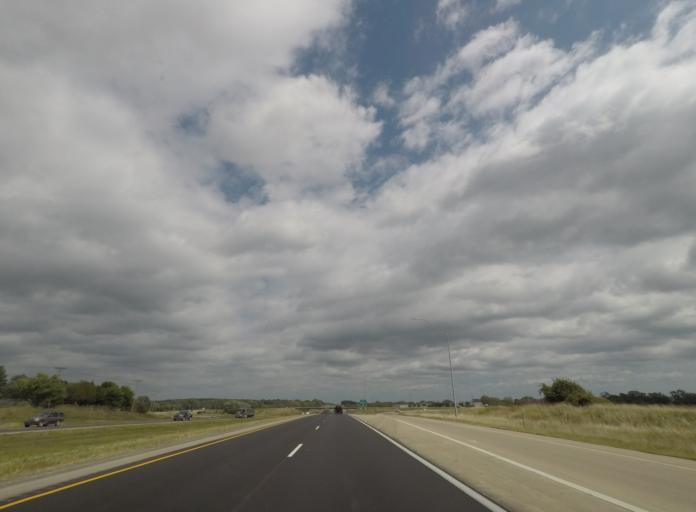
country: US
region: Iowa
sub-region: Linn County
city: Ely
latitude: 41.9266
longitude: -91.6447
